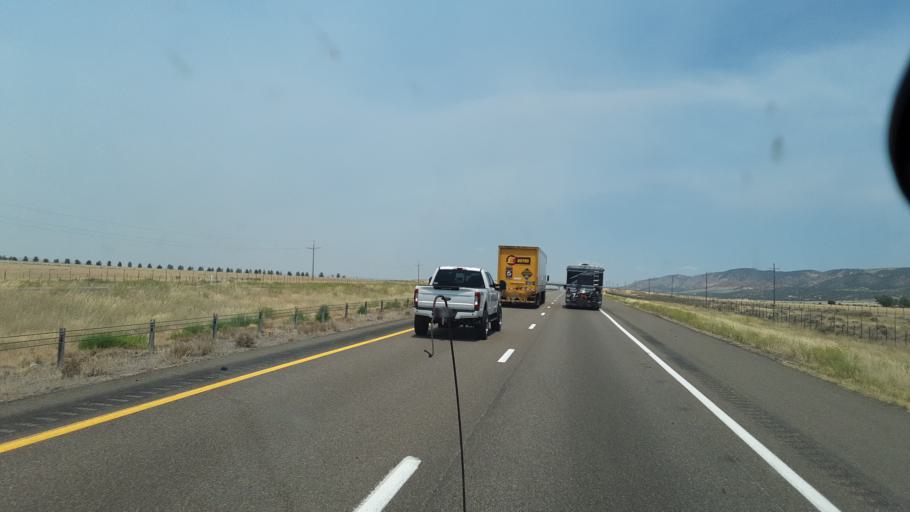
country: US
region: Utah
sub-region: Iron County
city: Cedar City
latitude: 37.5505
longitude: -113.1962
